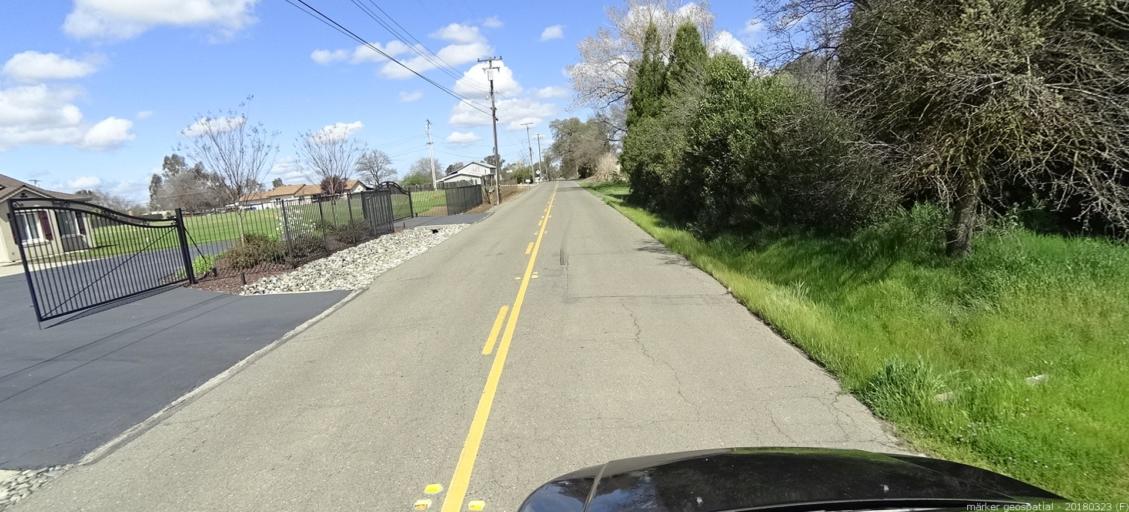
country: US
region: California
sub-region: Sacramento County
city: Rio Linda
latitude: 38.6881
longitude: -121.4245
